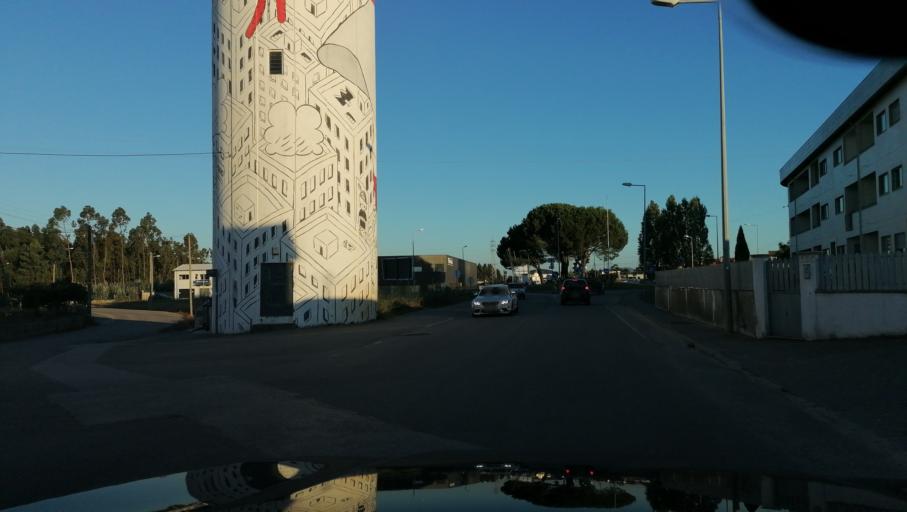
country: PT
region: Aveiro
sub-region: Agueda
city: Agueda
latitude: 40.5573
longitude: -8.4660
